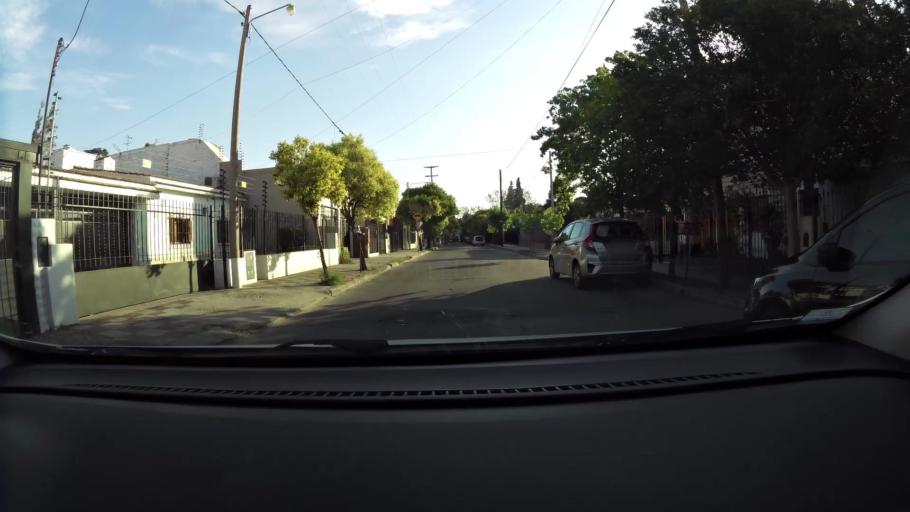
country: AR
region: Cordoba
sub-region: Departamento de Capital
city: Cordoba
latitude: -31.3857
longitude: -64.2229
